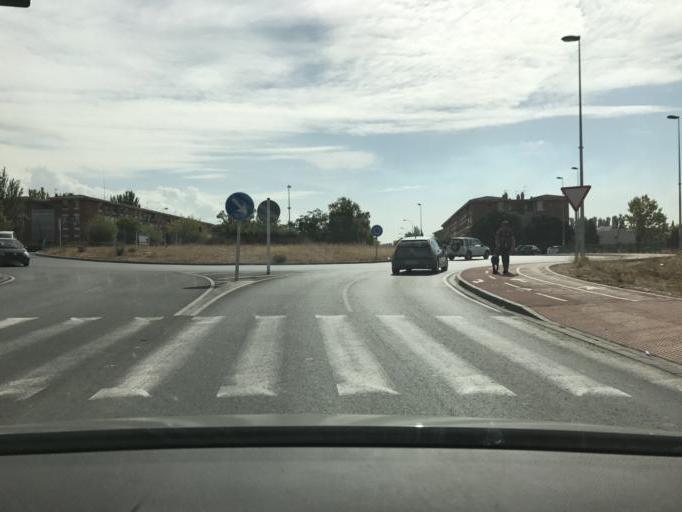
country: ES
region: Andalusia
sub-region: Provincia de Granada
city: Pulianas
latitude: 37.2124
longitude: -3.6146
